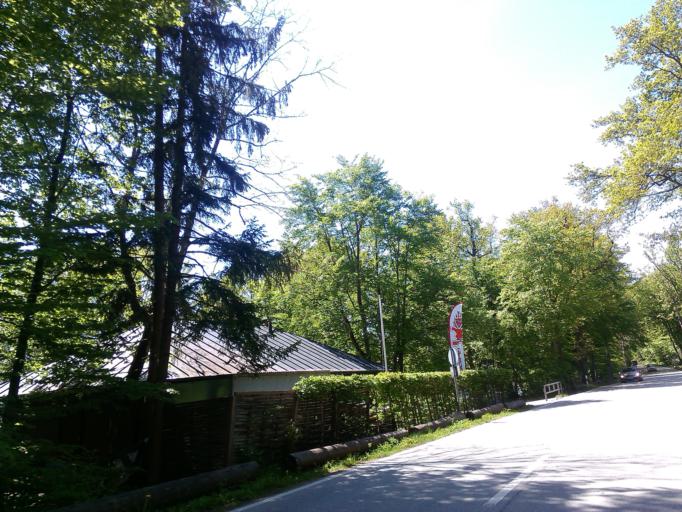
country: DE
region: Bavaria
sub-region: Upper Bavaria
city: Pocking
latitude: 47.9663
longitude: 11.3223
